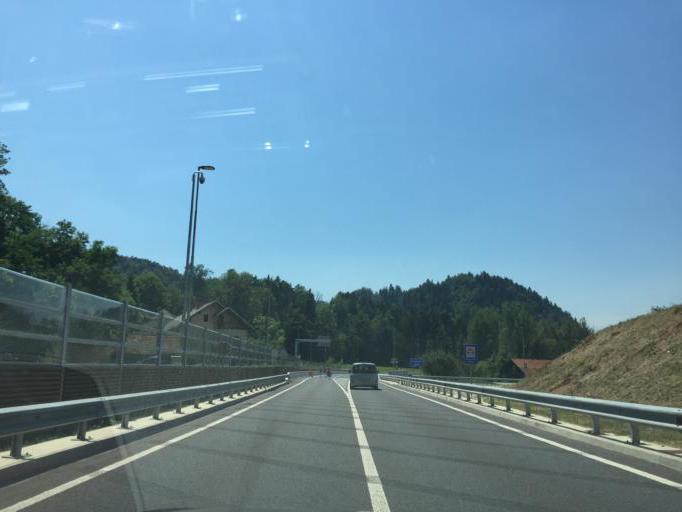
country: SI
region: Skofja Loka
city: Skofja Loka
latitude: 46.1579
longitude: 14.3113
